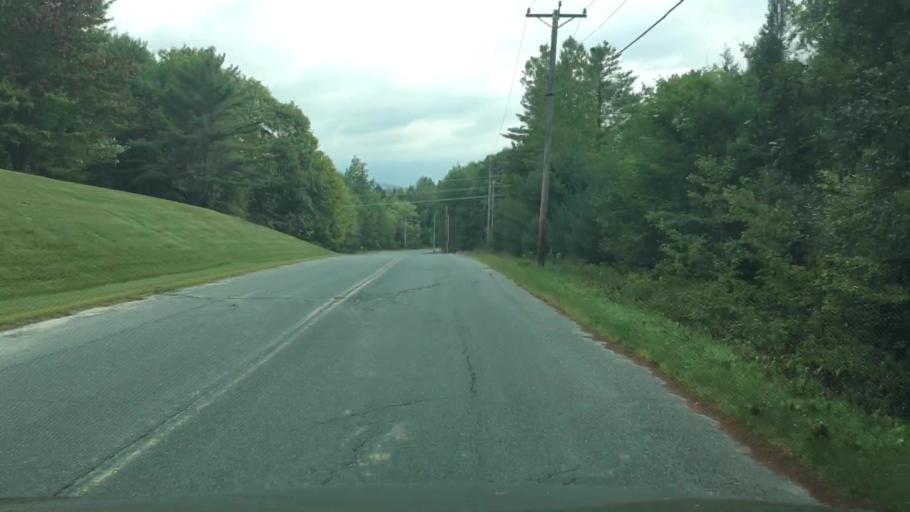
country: US
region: New Hampshire
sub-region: Grafton County
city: Littleton
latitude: 44.3225
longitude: -71.8767
